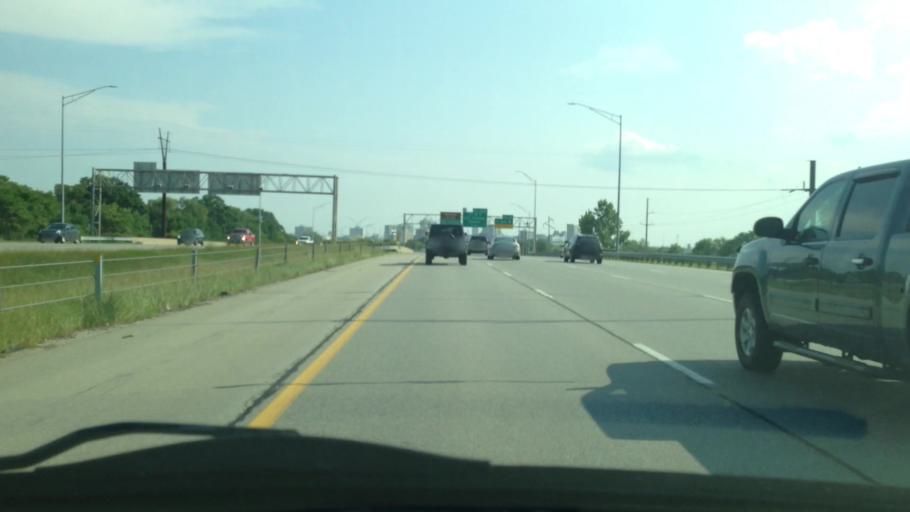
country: US
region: Iowa
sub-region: Linn County
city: Cedar Rapids
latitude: 42.0012
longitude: -91.6668
